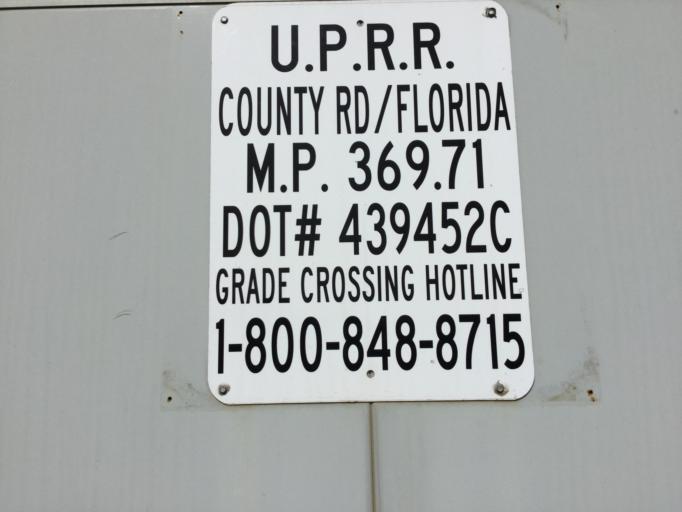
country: US
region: Kansas
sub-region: Anderson County
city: Garnett
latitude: 38.2065
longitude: -95.4255
